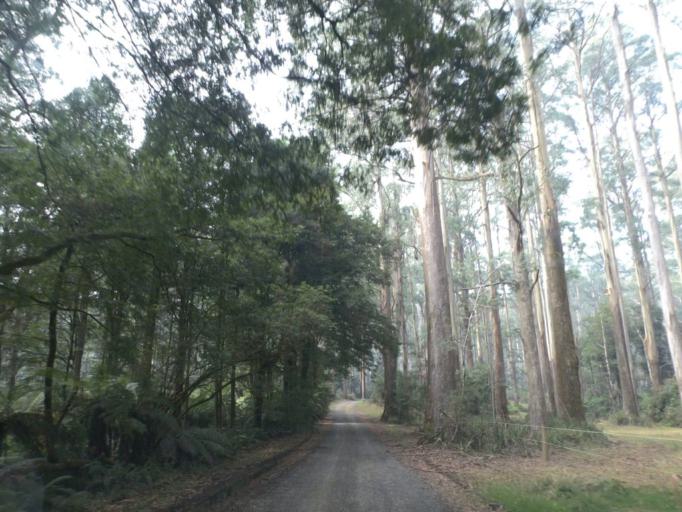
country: AU
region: Victoria
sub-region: Yarra Ranges
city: Healesville
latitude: -37.5572
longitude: 145.5335
